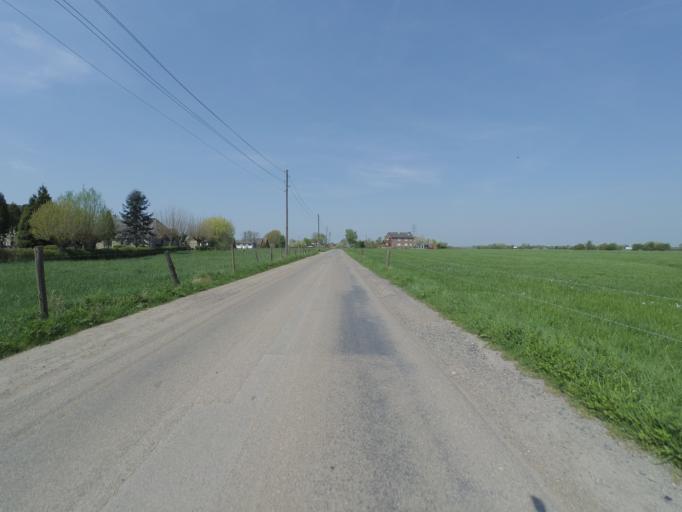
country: DE
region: North Rhine-Westphalia
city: Rees
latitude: 51.8186
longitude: 6.3915
